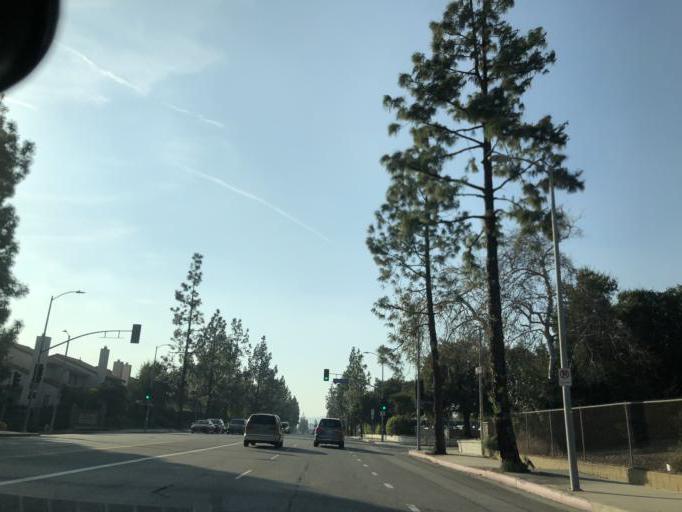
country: US
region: California
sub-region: Los Angeles County
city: Northridge
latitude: 34.2754
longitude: -118.5515
